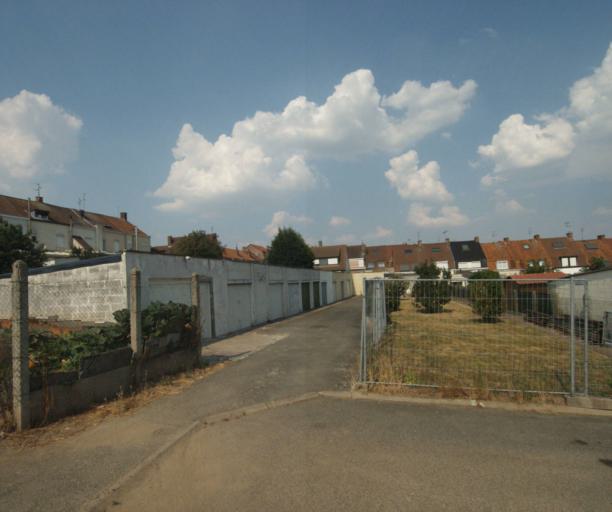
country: FR
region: Nord-Pas-de-Calais
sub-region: Departement du Nord
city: Linselles
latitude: 50.7350
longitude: 3.0794
